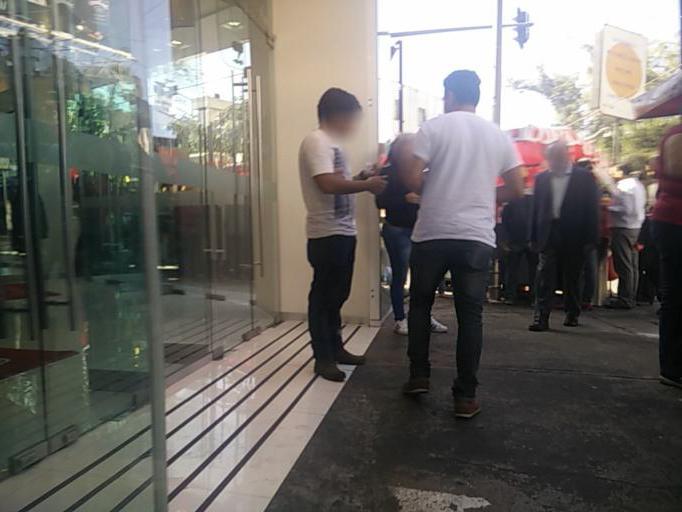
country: MX
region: Mexico City
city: Benito Juarez
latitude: 19.4131
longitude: -99.1659
